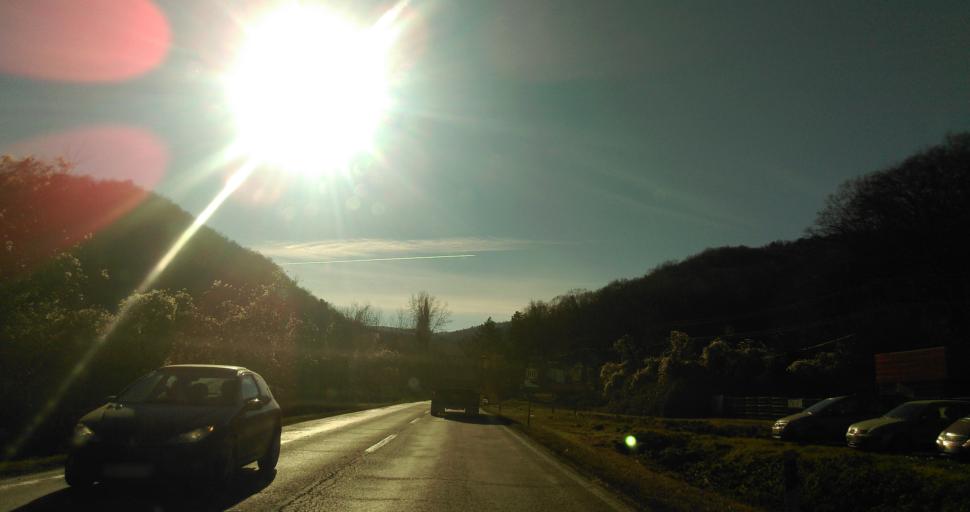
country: RS
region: Autonomna Pokrajina Vojvodina
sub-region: Juznobacki Okrug
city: Novi Sad
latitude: 45.1872
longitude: 19.8401
